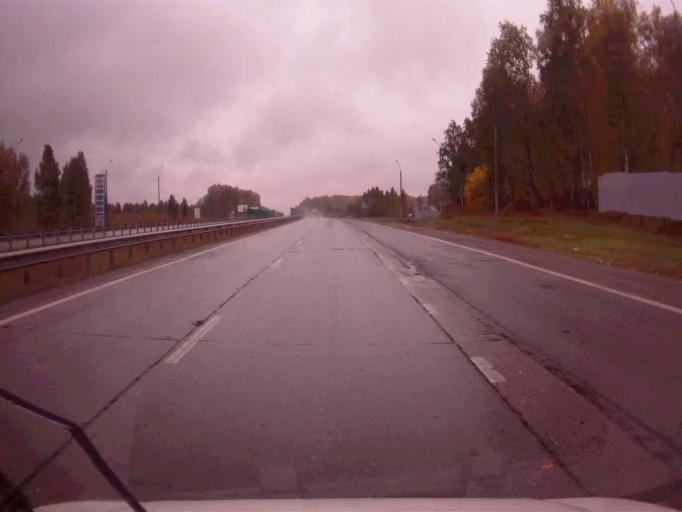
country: RU
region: Chelyabinsk
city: Dolgoderevenskoye
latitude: 55.3270
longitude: 61.3271
